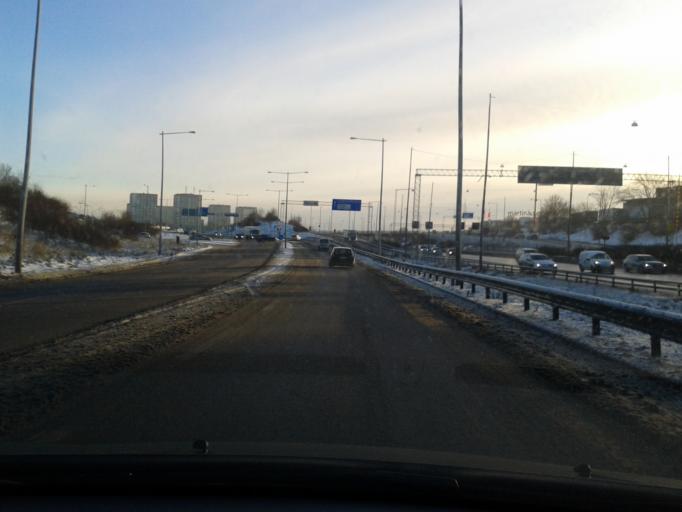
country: SE
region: Stockholm
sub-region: Stockholms Kommun
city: Arsta
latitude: 59.2976
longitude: 18.0316
